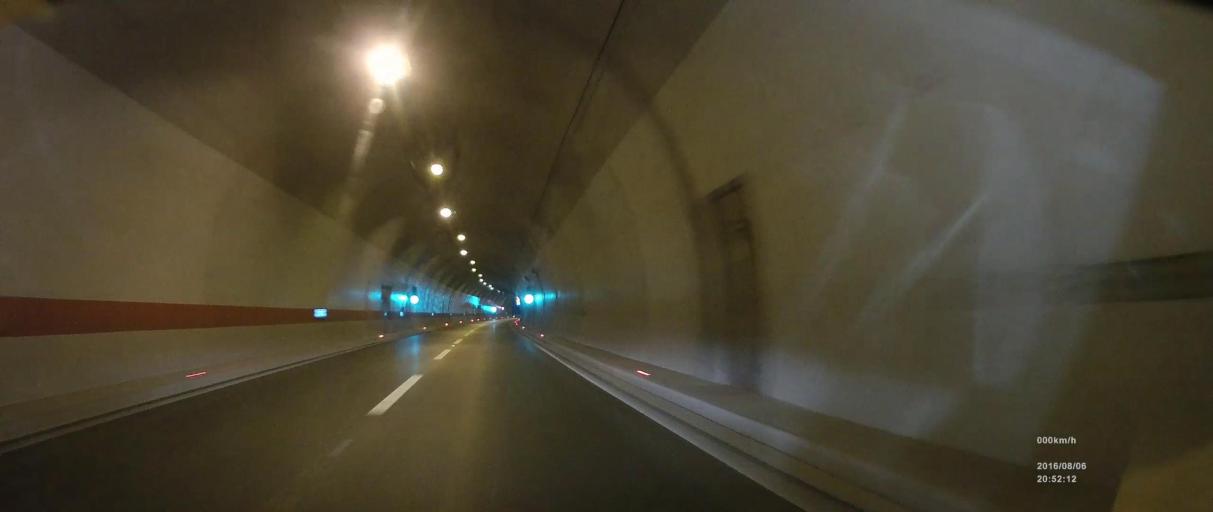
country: BA
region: Federation of Bosnia and Herzegovina
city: Ljubuski
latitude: 43.1256
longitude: 17.4850
